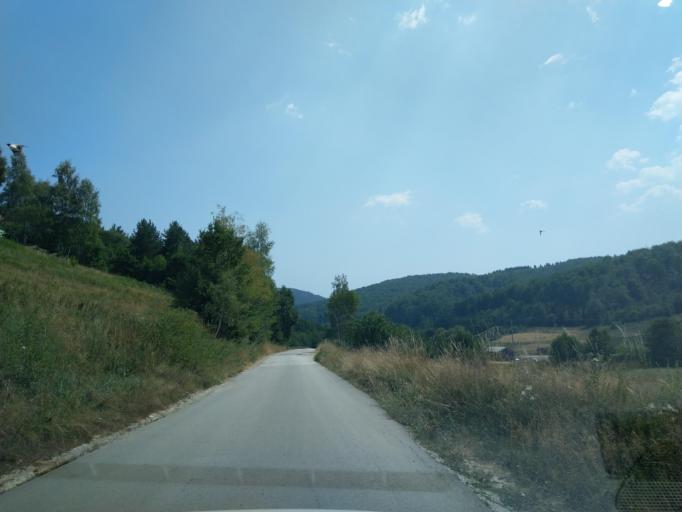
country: RS
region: Central Serbia
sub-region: Zlatiborski Okrug
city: Prijepolje
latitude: 43.3332
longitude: 19.5612
